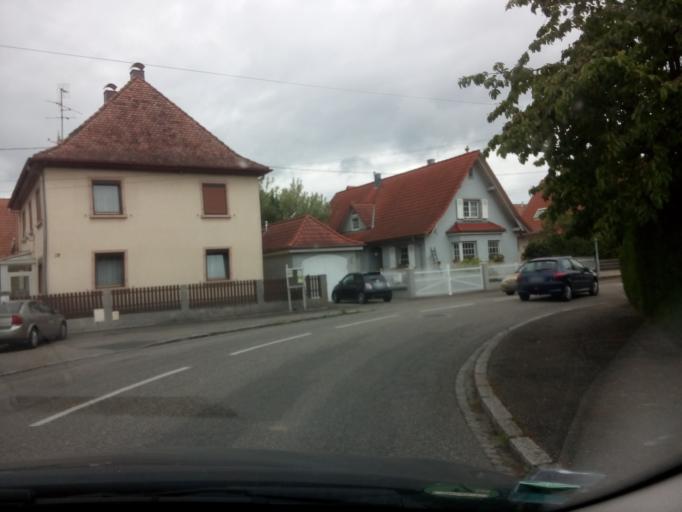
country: FR
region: Alsace
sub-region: Departement du Bas-Rhin
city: Soufflenheim
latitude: 48.8001
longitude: 7.9824
